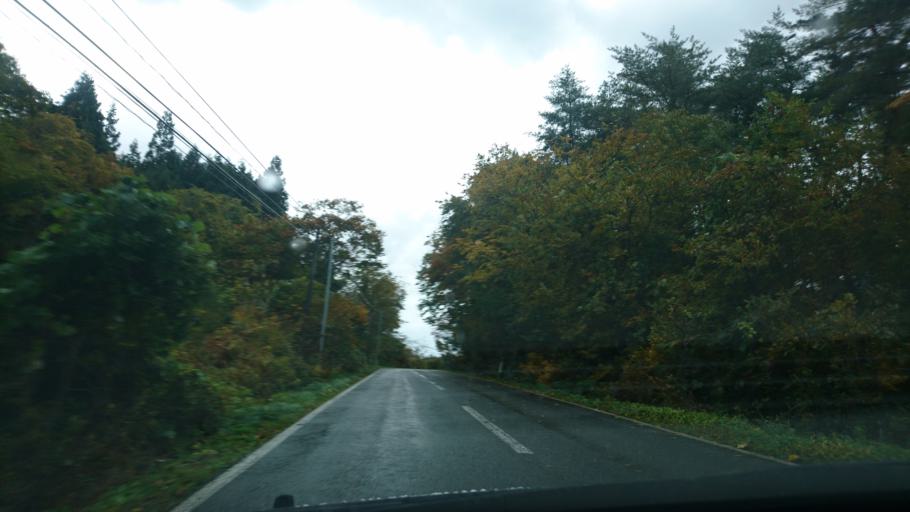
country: JP
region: Iwate
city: Shizukuishi
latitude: 39.6194
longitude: 140.9460
